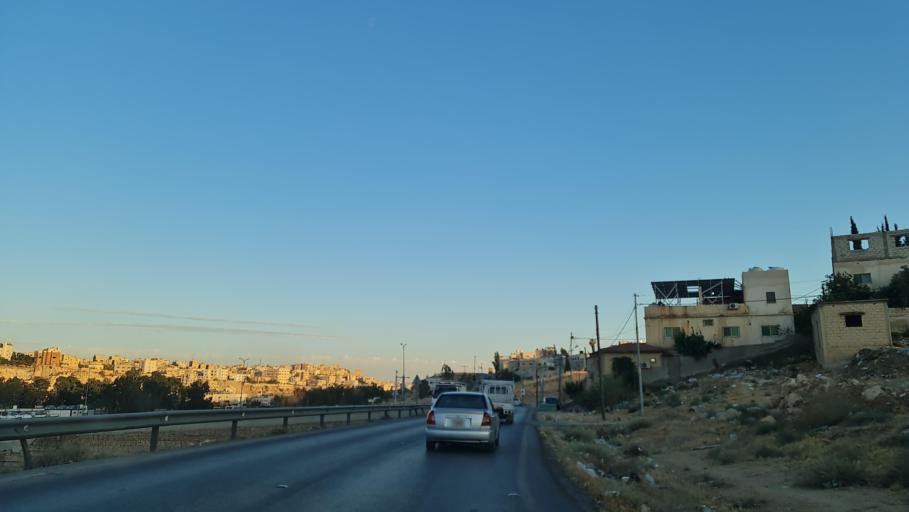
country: JO
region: Zarqa
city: Zarqa
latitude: 32.0820
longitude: 36.0658
